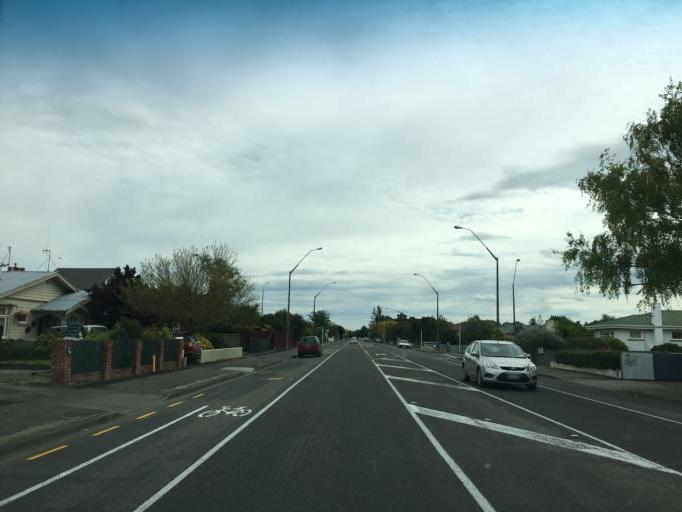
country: NZ
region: Manawatu-Wanganui
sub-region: Palmerston North City
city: Palmerston North
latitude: -40.3548
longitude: 175.5953
